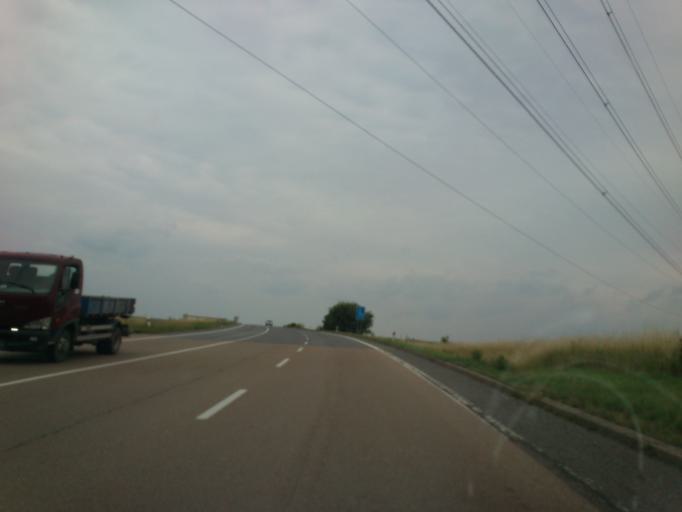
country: CZ
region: Central Bohemia
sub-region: Okres Mlada Boleslav
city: Mlada Boleslav
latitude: 50.4557
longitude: 14.8714
